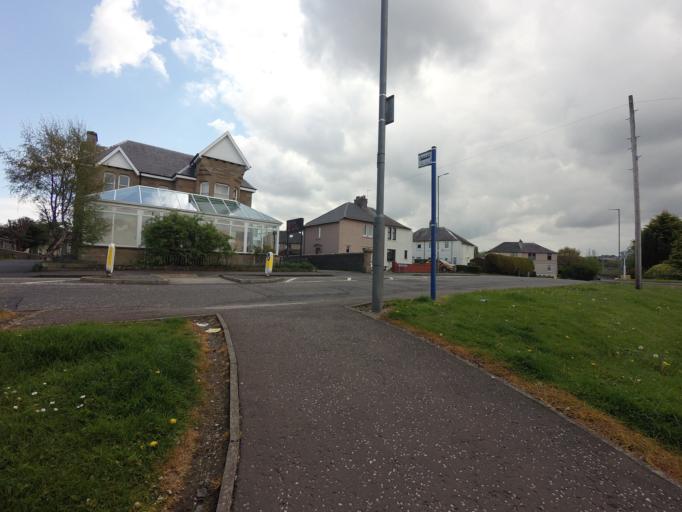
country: GB
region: Scotland
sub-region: Falkirk
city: Falkirk
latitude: 56.0097
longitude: -3.7962
